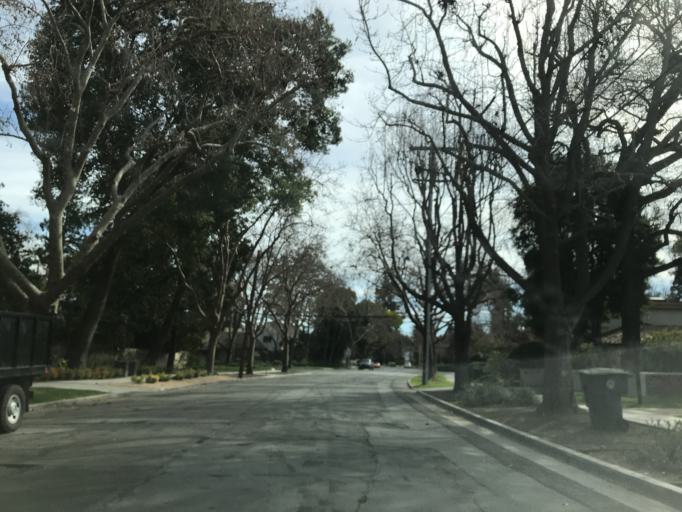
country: US
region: California
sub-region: Santa Clara County
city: Palo Alto
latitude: 37.4342
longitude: -122.1396
